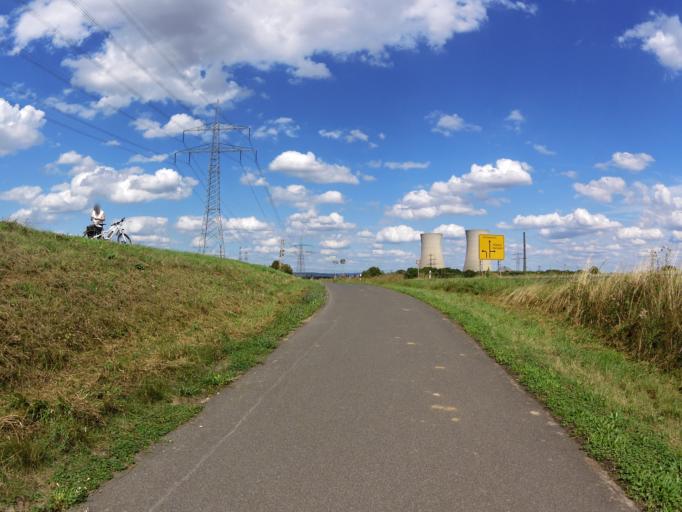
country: DE
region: Bavaria
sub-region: Regierungsbezirk Unterfranken
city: Bergrheinfeld
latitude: 49.9780
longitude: 10.1665
